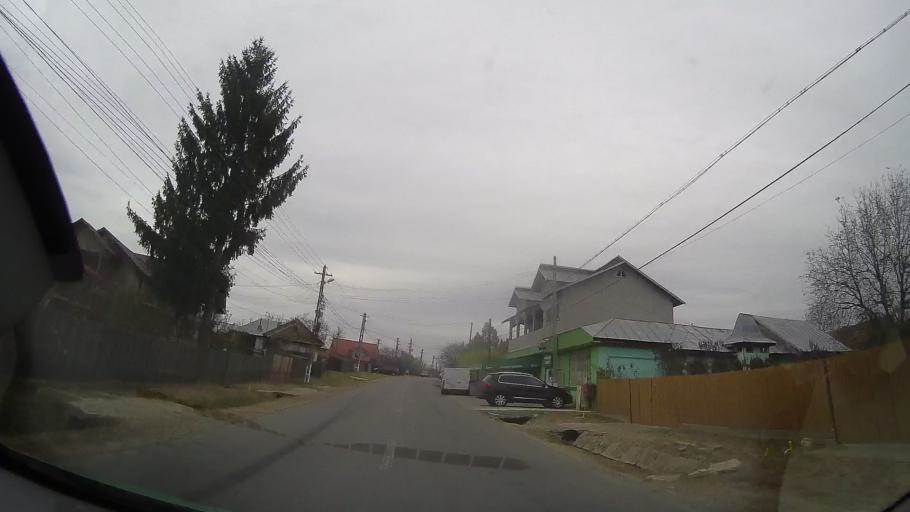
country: RO
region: Prahova
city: Mocesti
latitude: 45.0545
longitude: 26.2409
